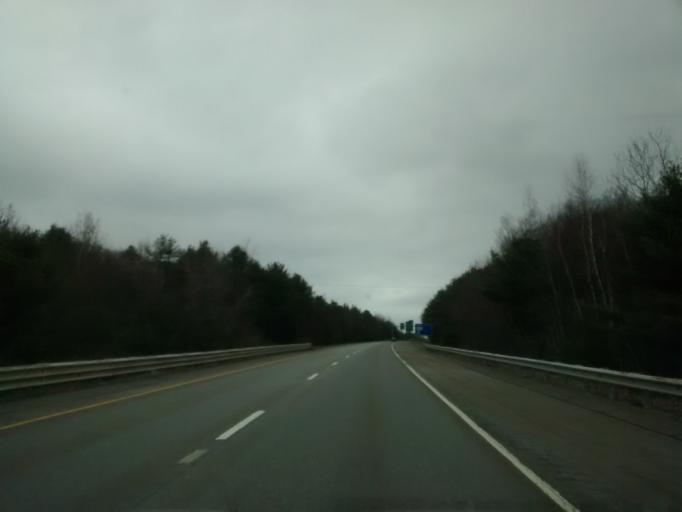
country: US
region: Massachusetts
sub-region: Worcester County
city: Phillipston
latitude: 42.5681
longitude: -72.1082
